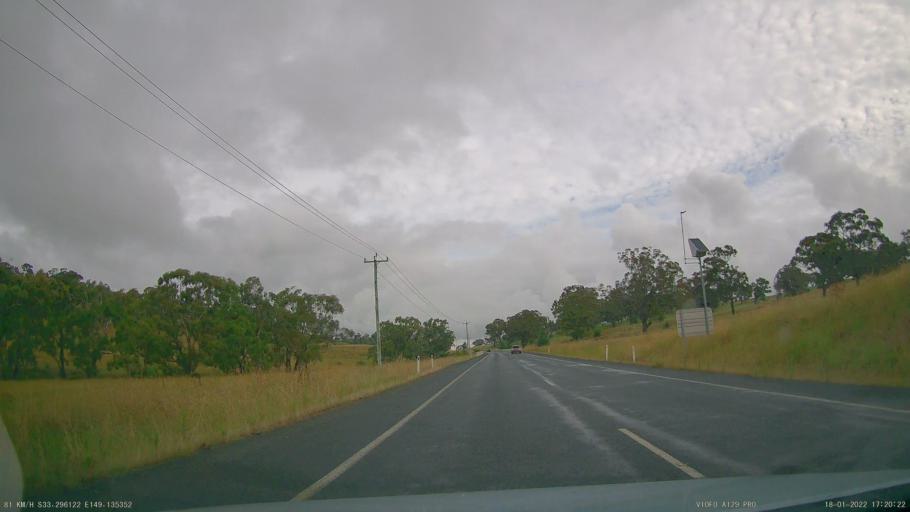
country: AU
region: New South Wales
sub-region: Orange Municipality
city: Orange
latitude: -33.2964
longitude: 149.1354
